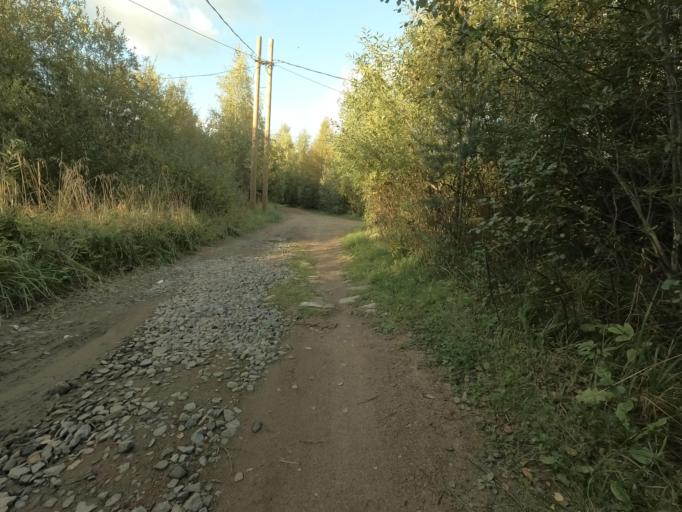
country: RU
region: Leningrad
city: Imeni Sverdlova
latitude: 59.8555
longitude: 30.7316
